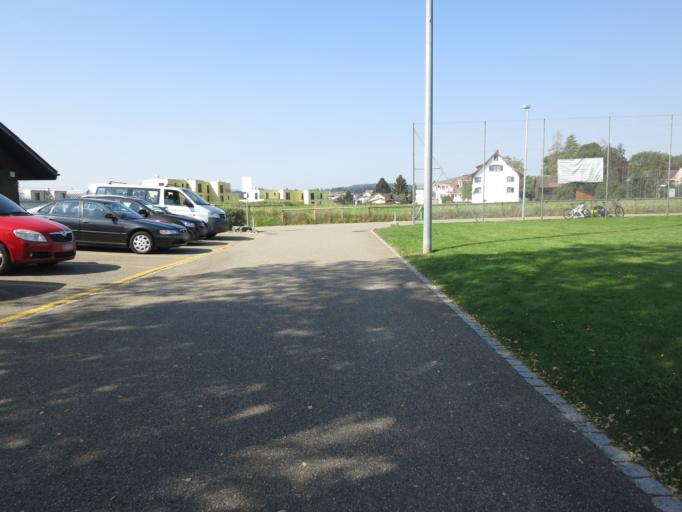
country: CH
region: Zurich
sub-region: Bezirk Meilen
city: Hombrechtikon
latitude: 47.2514
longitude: 8.7819
